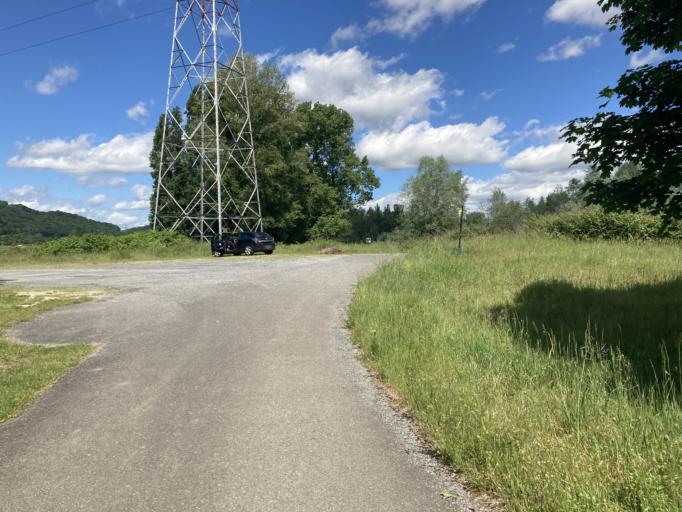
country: FR
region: Aquitaine
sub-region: Departement des Pyrenees-Atlantiques
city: Arbus
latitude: 43.3390
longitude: -0.4987
